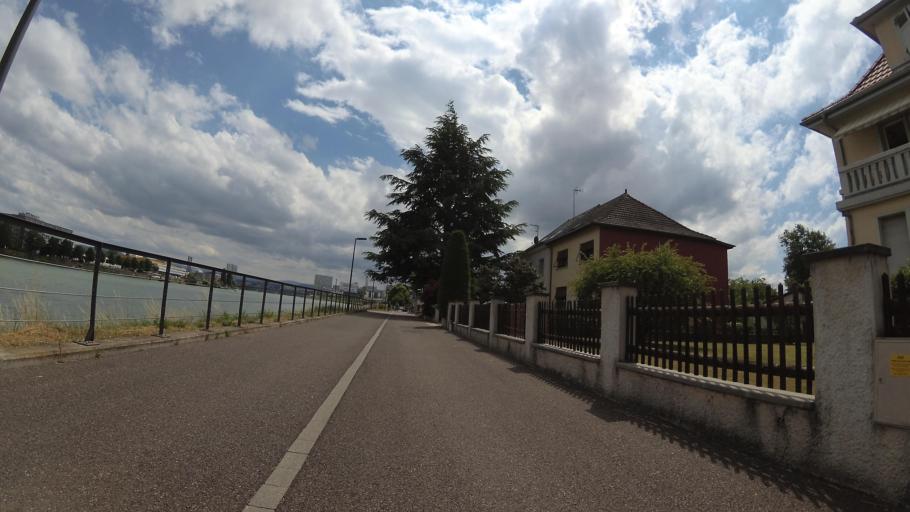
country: FR
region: Alsace
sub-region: Departement du Haut-Rhin
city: Village-Neuf
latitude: 47.5846
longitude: 7.5845
